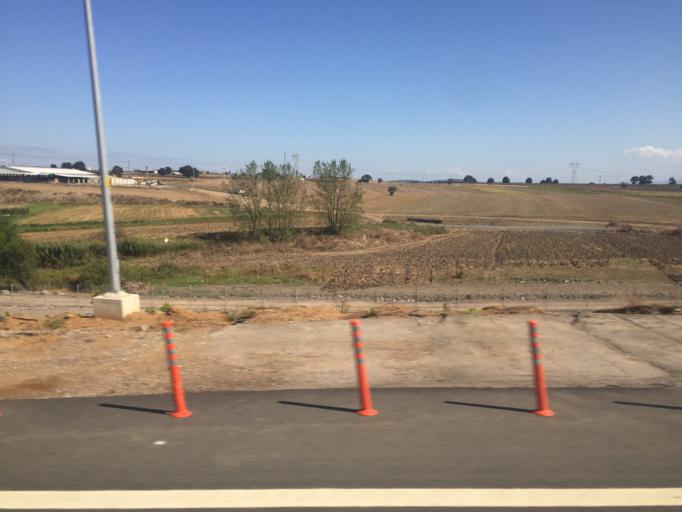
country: TR
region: Bursa
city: Mahmudiye
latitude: 40.2725
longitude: 28.6055
